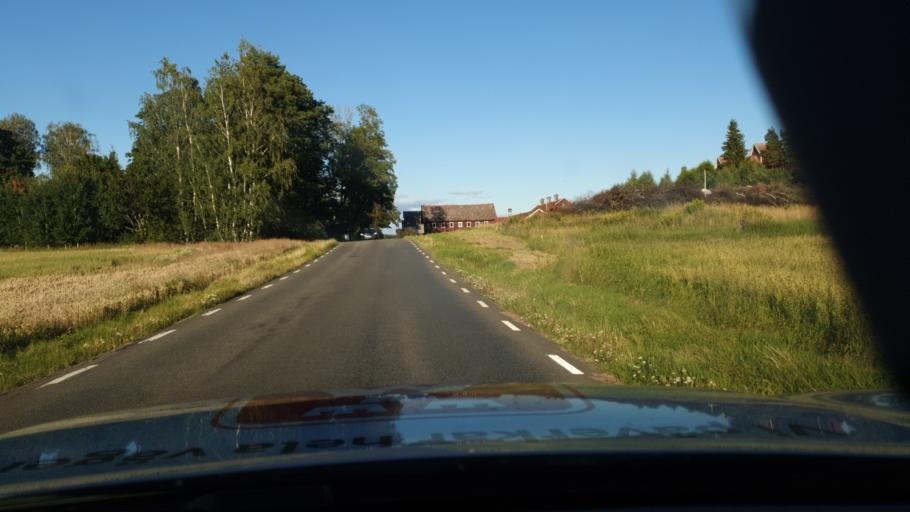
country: SE
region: Vaestra Goetaland
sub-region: Skovde Kommun
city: Stopen
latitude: 58.4742
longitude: 13.9354
